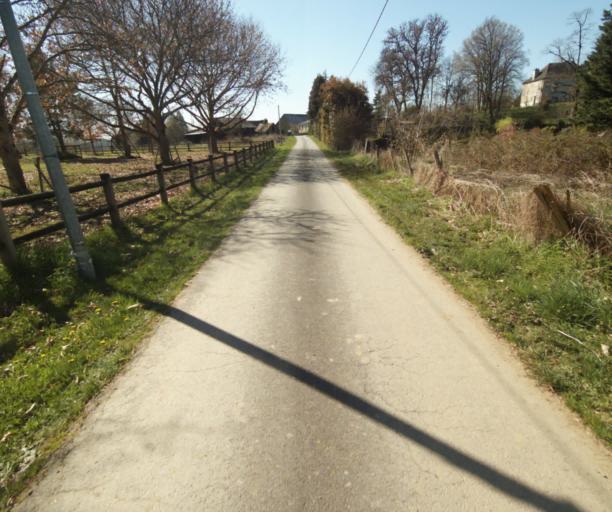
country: FR
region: Limousin
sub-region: Departement de la Correze
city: Saint-Mexant
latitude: 45.2944
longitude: 1.6069
